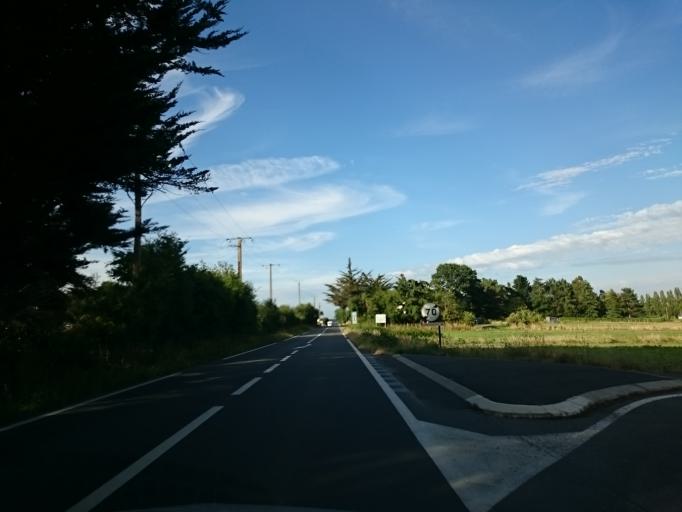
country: FR
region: Brittany
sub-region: Departement d'Ille-et-Vilaine
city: Bain-de-Bretagne
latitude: 47.8553
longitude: -1.6767
